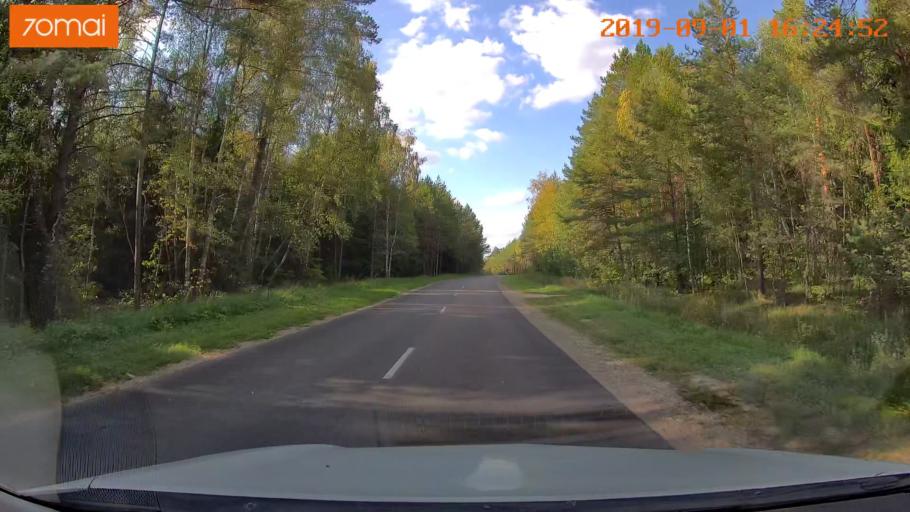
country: RU
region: Kaluga
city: Maloyaroslavets
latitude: 54.8958
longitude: 36.5193
